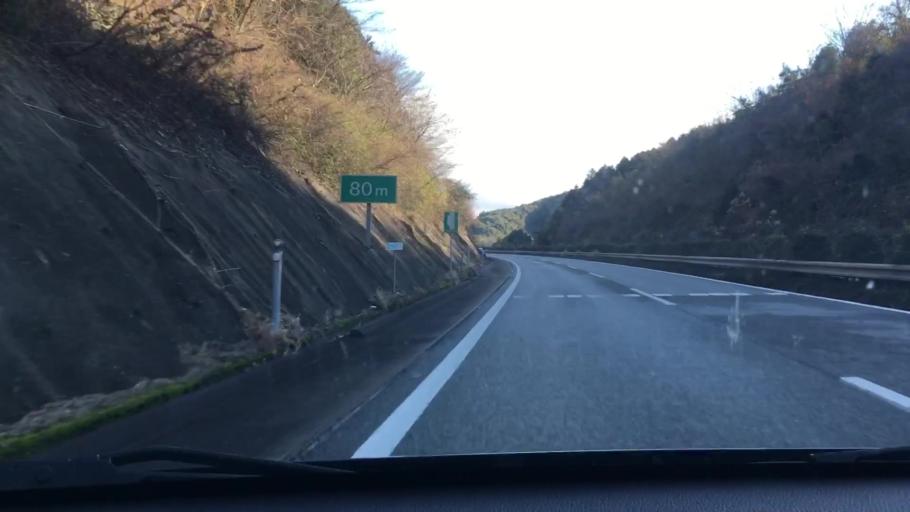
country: JP
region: Kumamoto
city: Hitoyoshi
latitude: 32.1733
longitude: 130.7903
